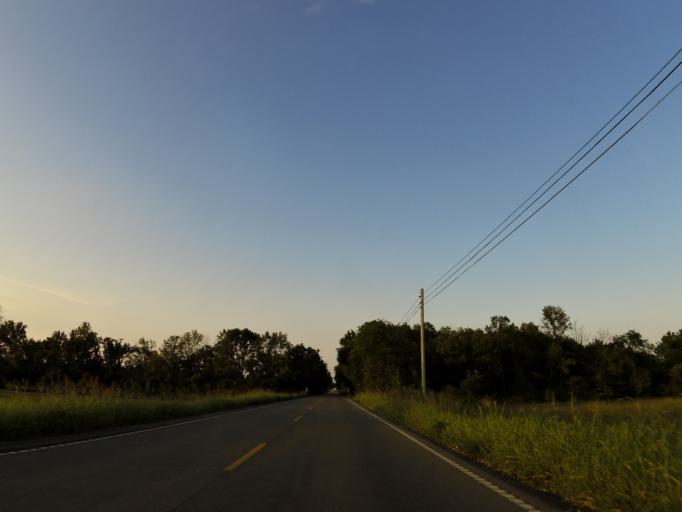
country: US
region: Tennessee
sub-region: Monroe County
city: Sweetwater
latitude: 35.6656
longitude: -84.4113
